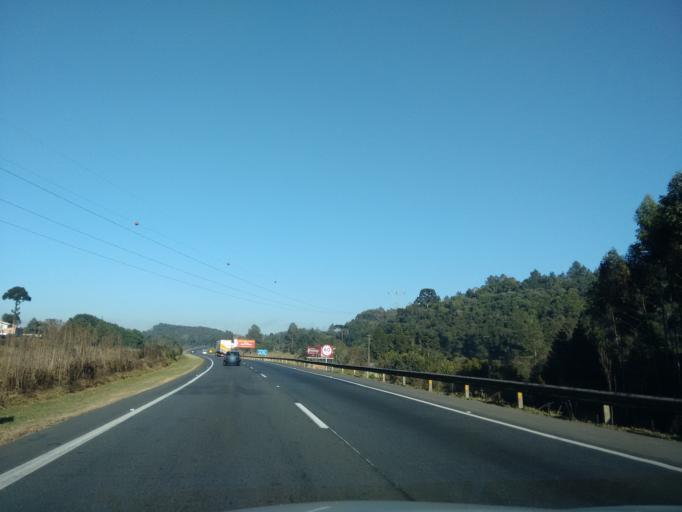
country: BR
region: Parana
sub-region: Campo Largo
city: Campo Largo
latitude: -25.4484
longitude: -49.5811
